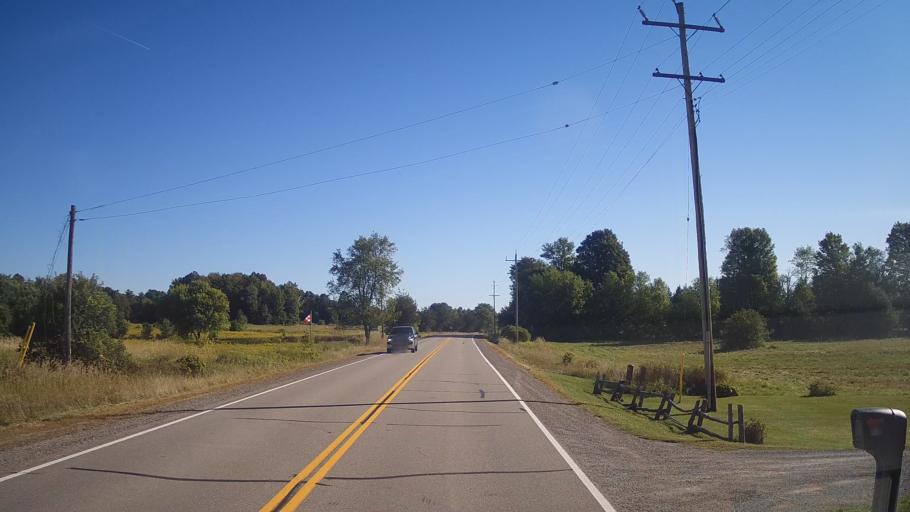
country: CA
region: Ontario
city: Gananoque
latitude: 44.5870
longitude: -76.1061
